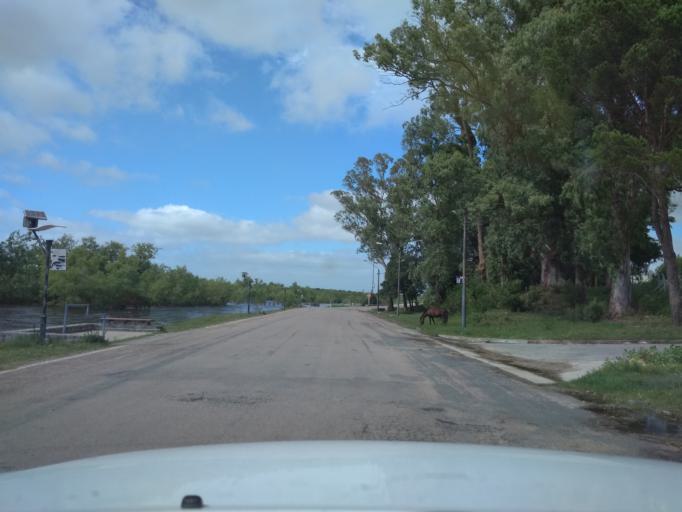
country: UY
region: Florida
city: Florida
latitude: -34.1066
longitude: -56.2050
